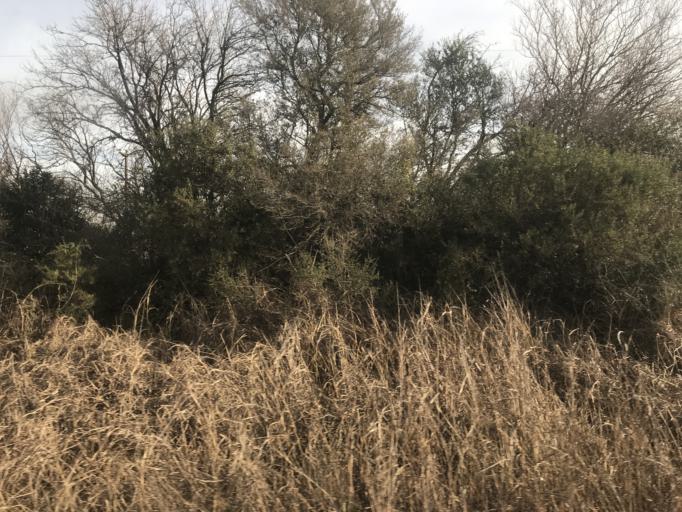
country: AR
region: Cordoba
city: Laguna Larga
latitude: -31.7547
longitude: -63.8225
